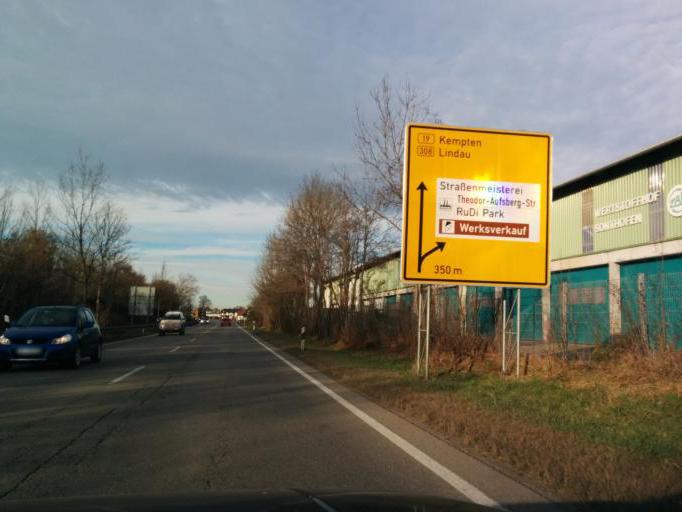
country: DE
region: Bavaria
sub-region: Swabia
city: Sonthofen
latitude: 47.5130
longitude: 10.2713
